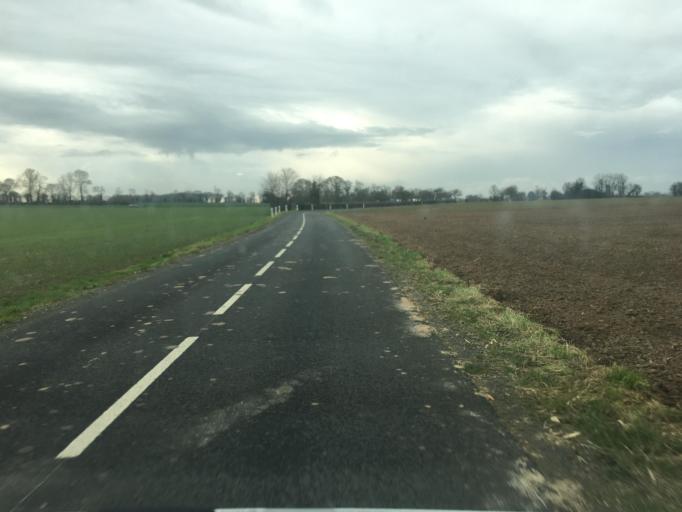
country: FR
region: Lower Normandy
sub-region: Departement du Calvados
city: Saint-Vigor-le-Grand
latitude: 49.3334
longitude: -0.6678
